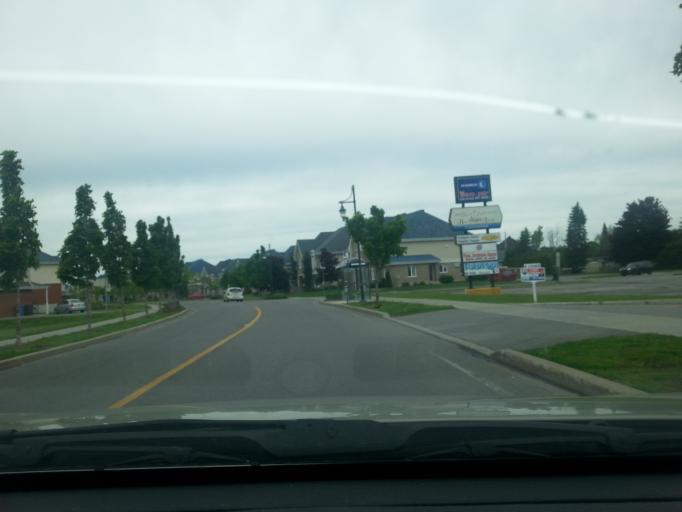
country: CA
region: Quebec
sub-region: Lanaudiere
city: Terrebonne
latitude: 45.6954
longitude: -73.6118
